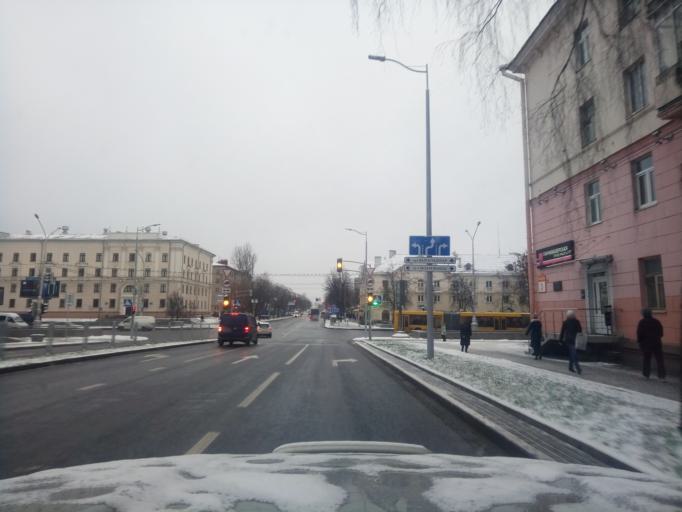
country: BY
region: Minsk
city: Minsk
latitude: 53.9270
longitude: 27.6269
